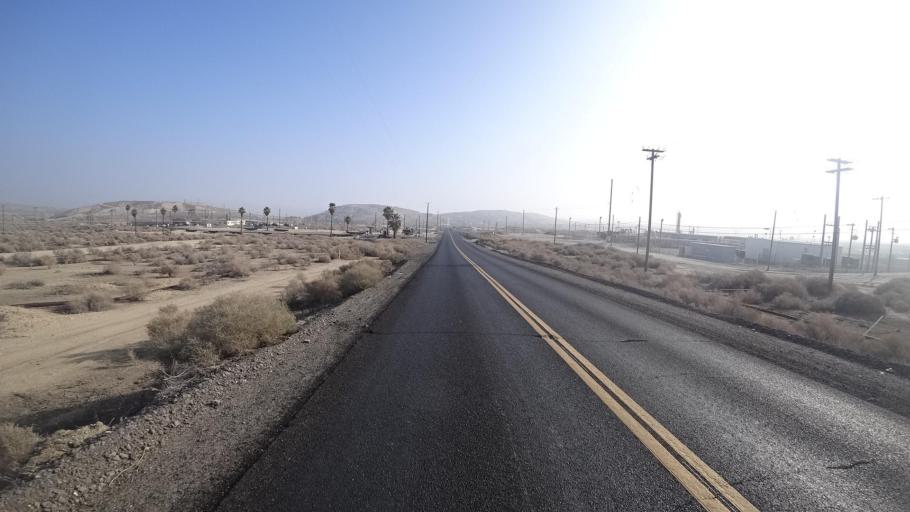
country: US
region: California
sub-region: Kern County
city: Ford City
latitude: 35.1806
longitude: -119.4624
